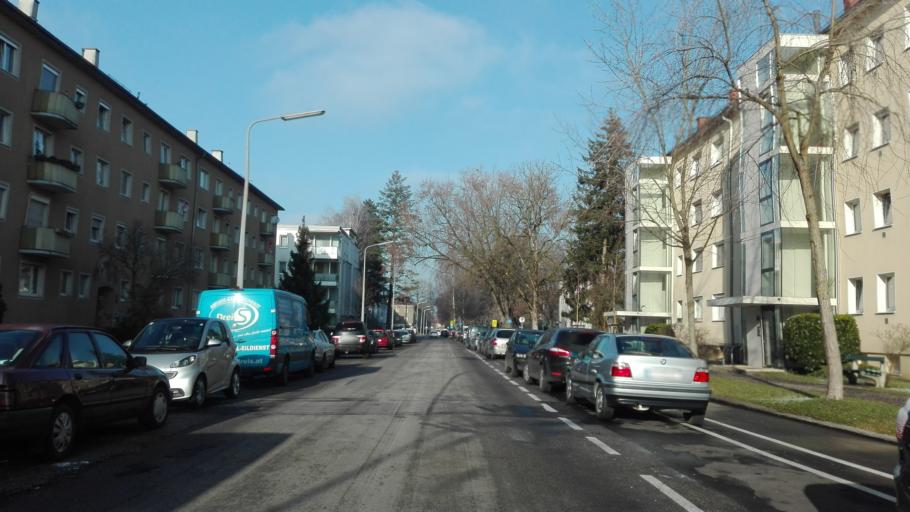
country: AT
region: Upper Austria
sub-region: Linz Stadt
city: Linz
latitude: 48.2703
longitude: 14.2882
